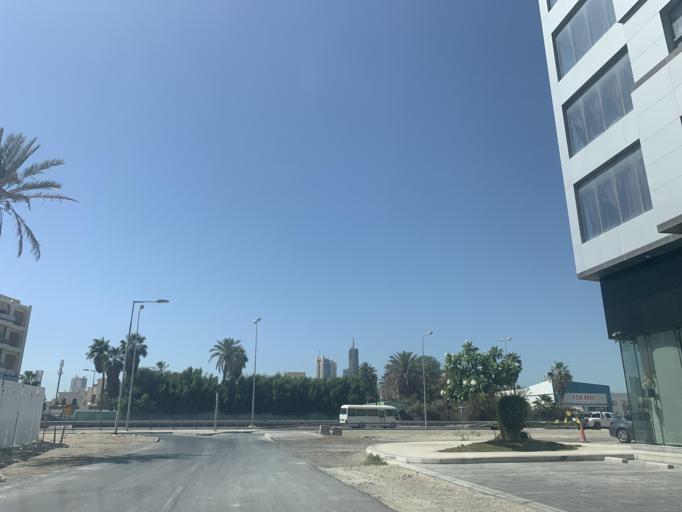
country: BH
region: Manama
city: Jidd Hafs
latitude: 26.2148
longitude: 50.5621
